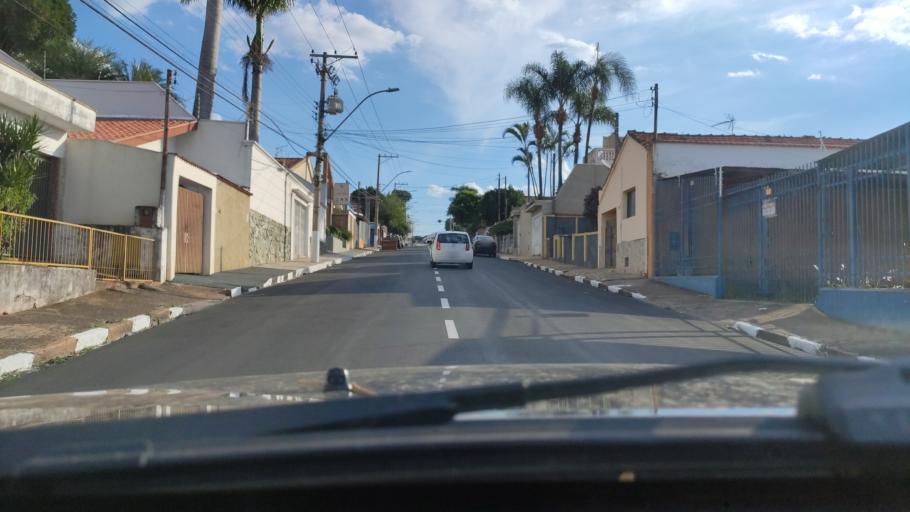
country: BR
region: Sao Paulo
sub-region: Itapira
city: Itapira
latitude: -22.4418
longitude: -46.8285
